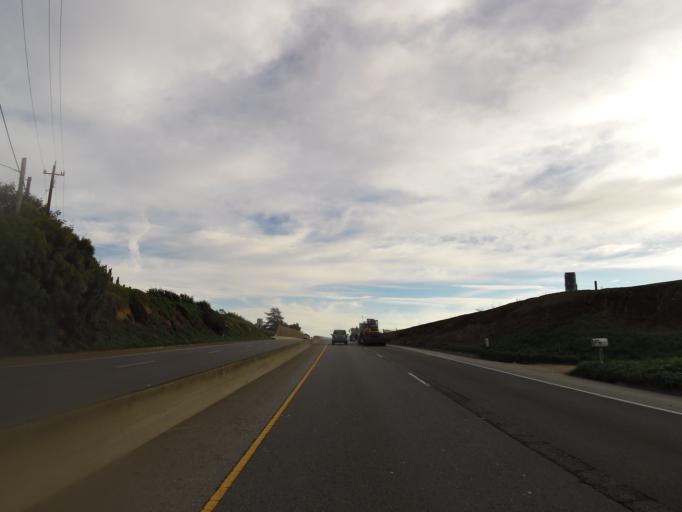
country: US
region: California
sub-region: Monterey County
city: Prunedale
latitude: 36.7534
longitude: -121.6642
